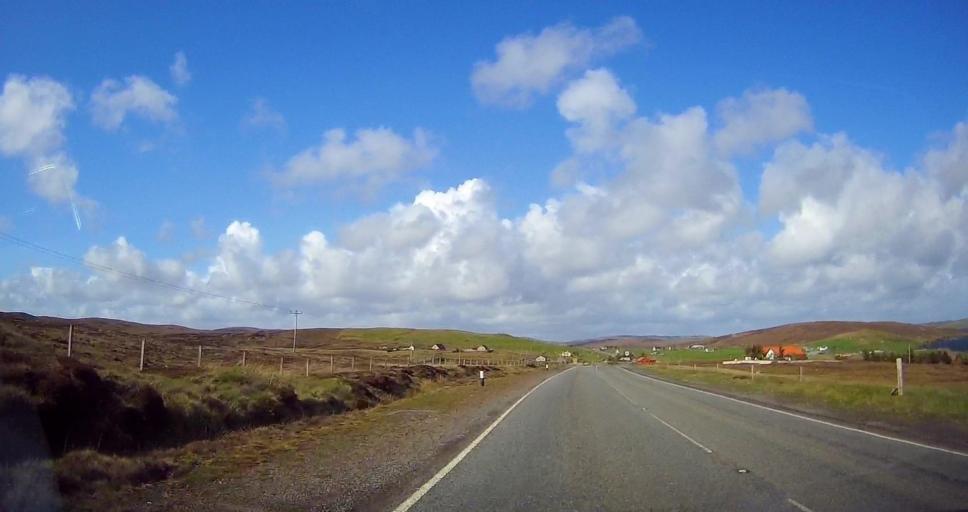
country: GB
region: Scotland
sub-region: Shetland Islands
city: Lerwick
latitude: 60.2304
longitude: -1.2372
